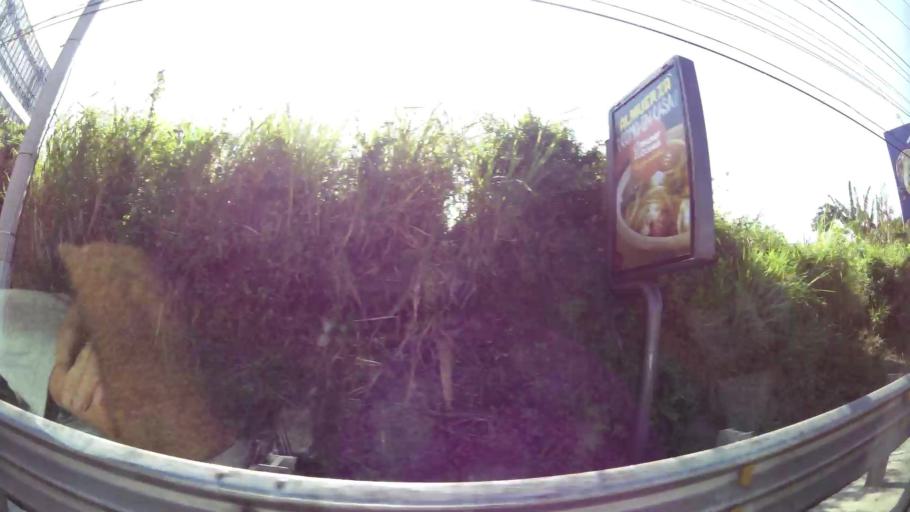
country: SV
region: La Libertad
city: Antiguo Cuscatlan
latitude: 13.6767
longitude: -89.2514
